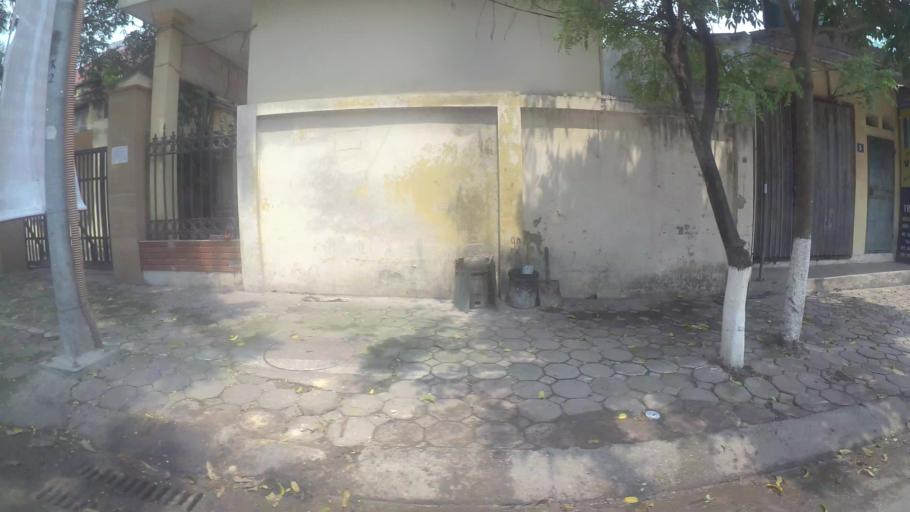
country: VN
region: Ha Noi
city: Tay Ho
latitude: 21.0890
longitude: 105.8087
